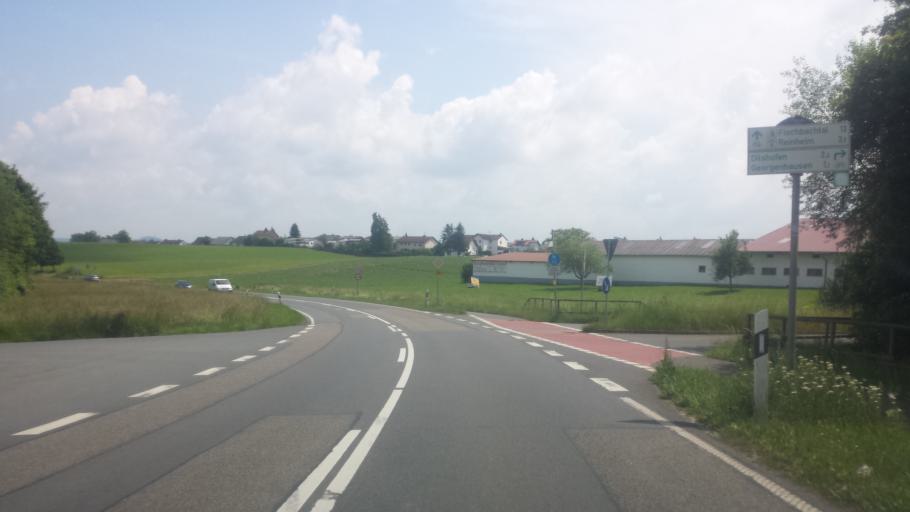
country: DE
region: Hesse
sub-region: Regierungsbezirk Darmstadt
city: Rossdorf
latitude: 49.8506
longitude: 8.8001
